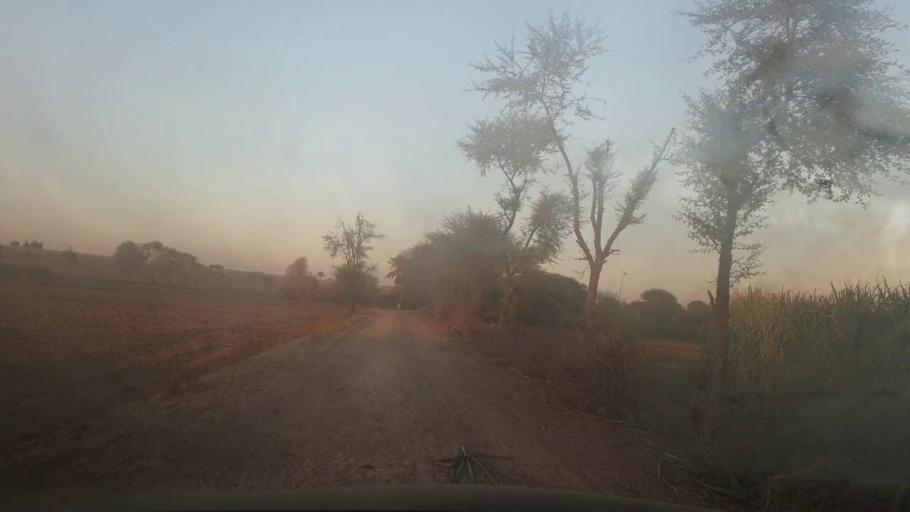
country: PK
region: Sindh
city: Ghotki
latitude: 28.0579
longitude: 69.3676
